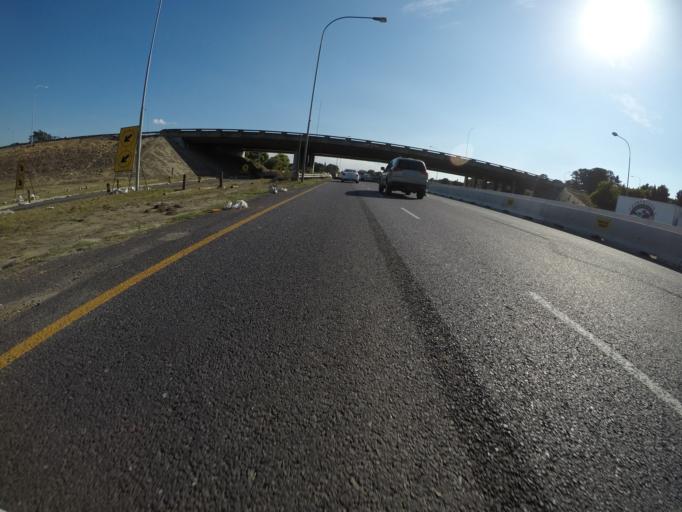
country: ZA
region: Western Cape
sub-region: City of Cape Town
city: Kraaifontein
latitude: -33.8767
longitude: 18.6597
